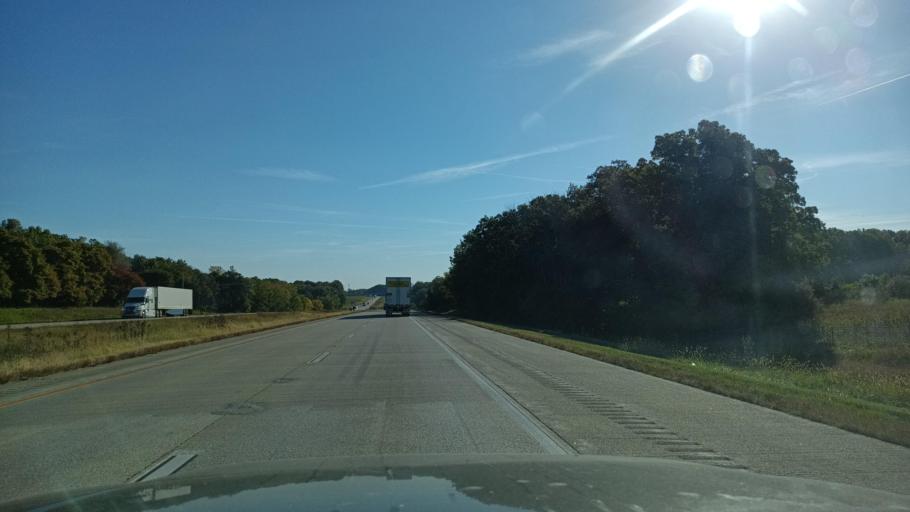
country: US
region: Illinois
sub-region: Clark County
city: Marshall
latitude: 39.4254
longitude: -87.6001
